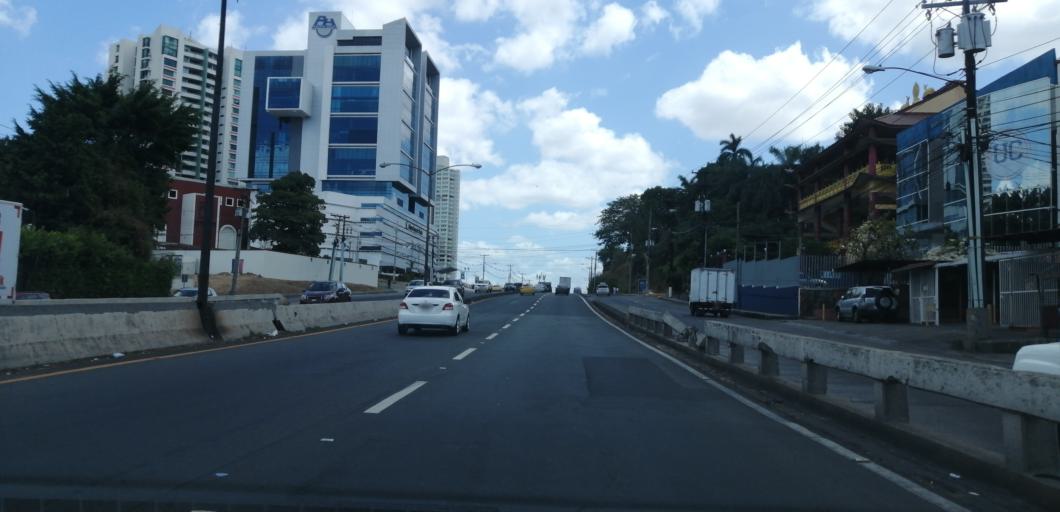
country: PA
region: Panama
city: Panama
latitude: 8.9901
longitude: -79.5318
